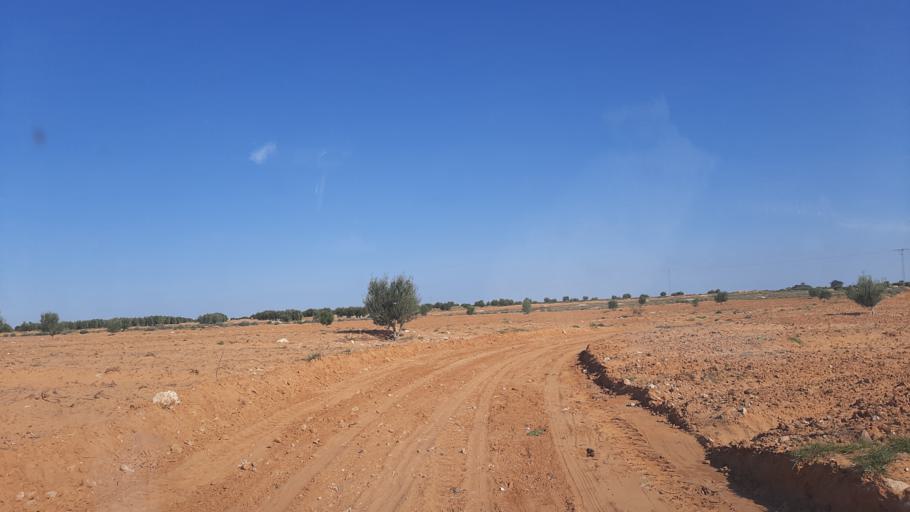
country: TN
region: Madanin
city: Medenine
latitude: 33.2816
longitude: 10.7797
